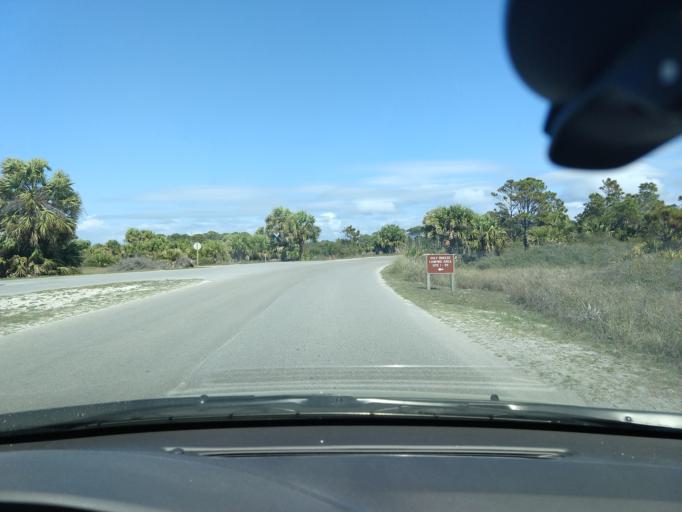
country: US
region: Florida
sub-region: Gulf County
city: Port Saint Joe
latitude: 29.7710
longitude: -85.4056
